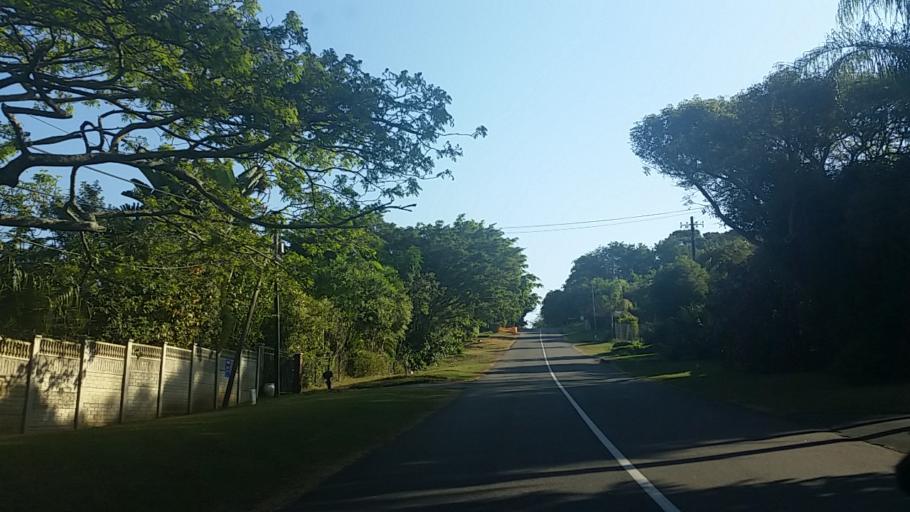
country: ZA
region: KwaZulu-Natal
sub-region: eThekwini Metropolitan Municipality
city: Berea
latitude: -29.8513
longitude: 30.9129
